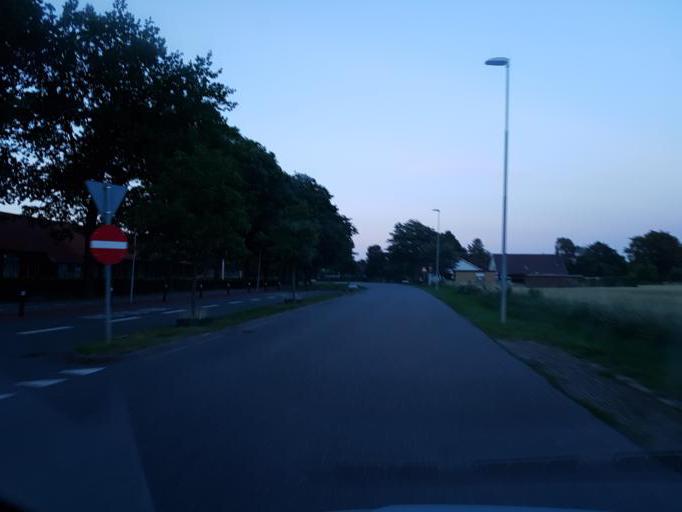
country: DK
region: South Denmark
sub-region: Vejen Kommune
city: Vejen
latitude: 55.4700
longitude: 9.0823
